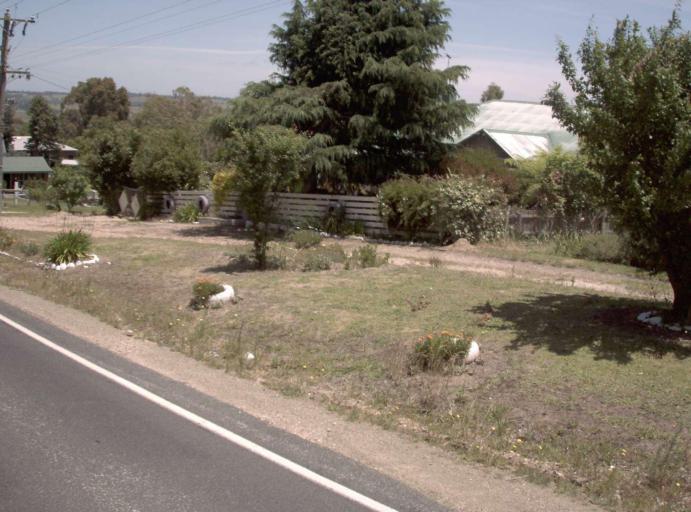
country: AU
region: Victoria
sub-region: East Gippsland
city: Lakes Entrance
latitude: -37.6989
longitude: 147.8363
